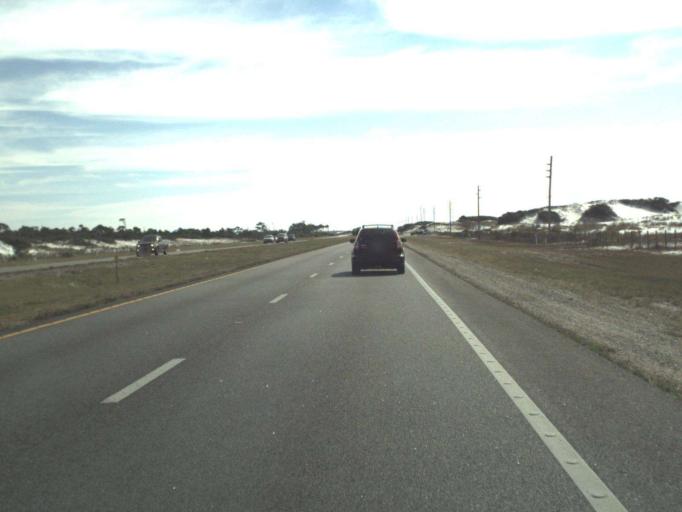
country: US
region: Florida
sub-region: Okaloosa County
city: Lake Lorraine
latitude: 30.3929
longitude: -86.5504
